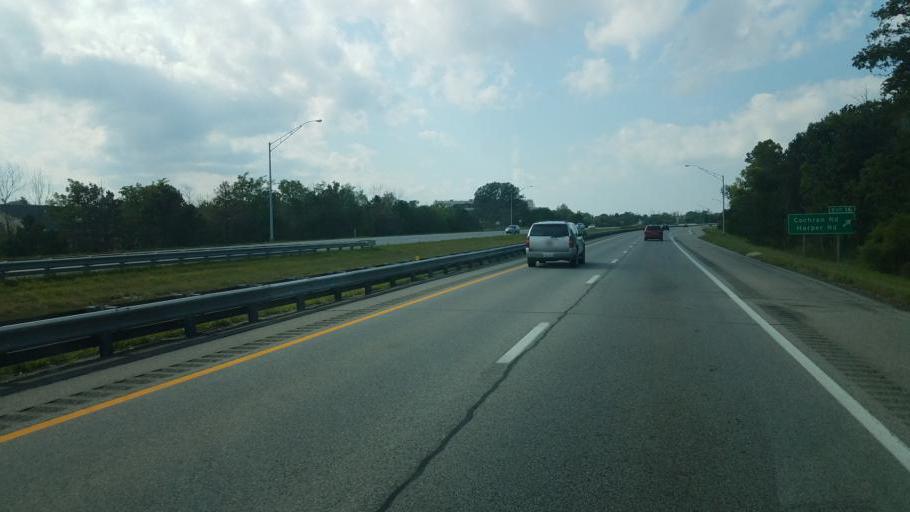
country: US
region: Ohio
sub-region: Cuyahoga County
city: Solon
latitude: 41.4024
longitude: -81.4609
